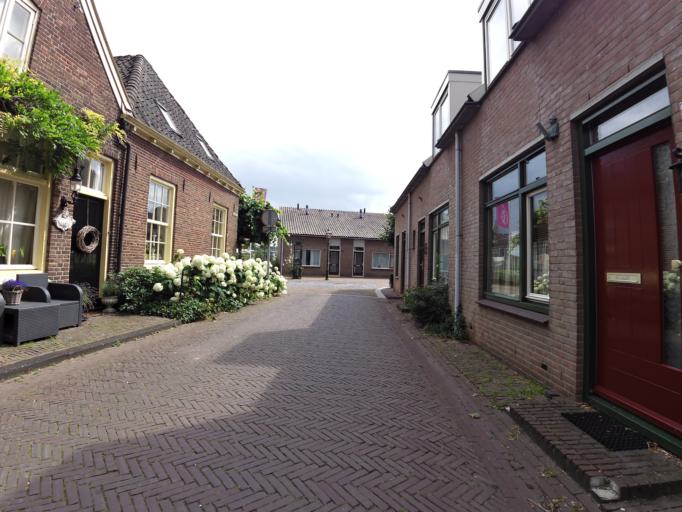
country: NL
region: Gelderland
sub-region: Gemeente Doesburg
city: Doesburg
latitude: 52.0134
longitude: 6.1326
